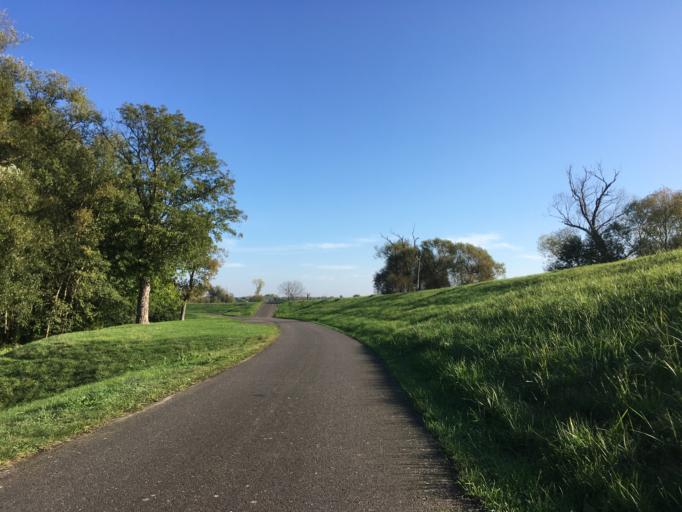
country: DE
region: Brandenburg
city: Reitwein
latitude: 52.5215
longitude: 14.6025
